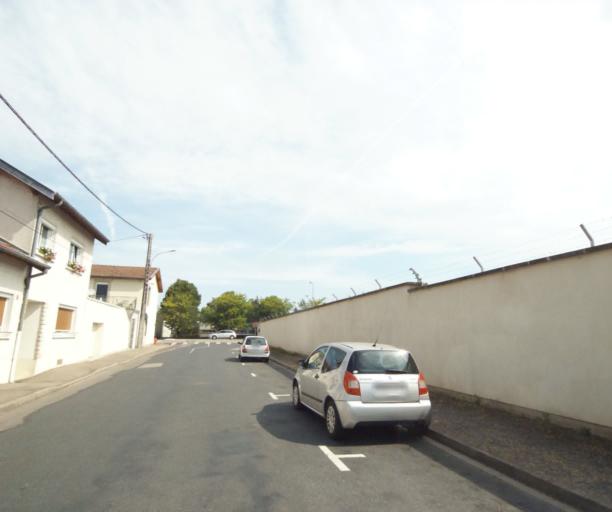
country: FR
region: Lorraine
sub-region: Departement de Meurthe-et-Moselle
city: Luneville
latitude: 48.5916
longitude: 6.5107
